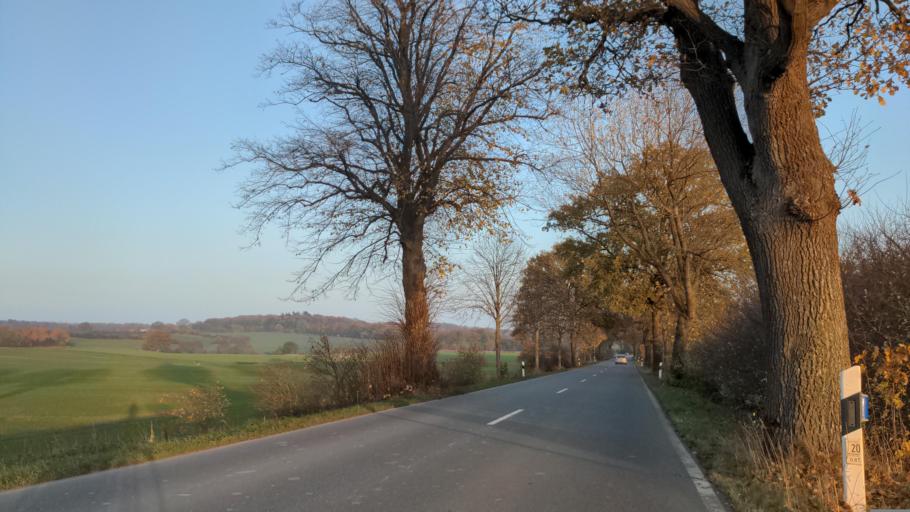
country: DE
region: Schleswig-Holstein
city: Glasau
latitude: 54.0920
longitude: 10.5044
